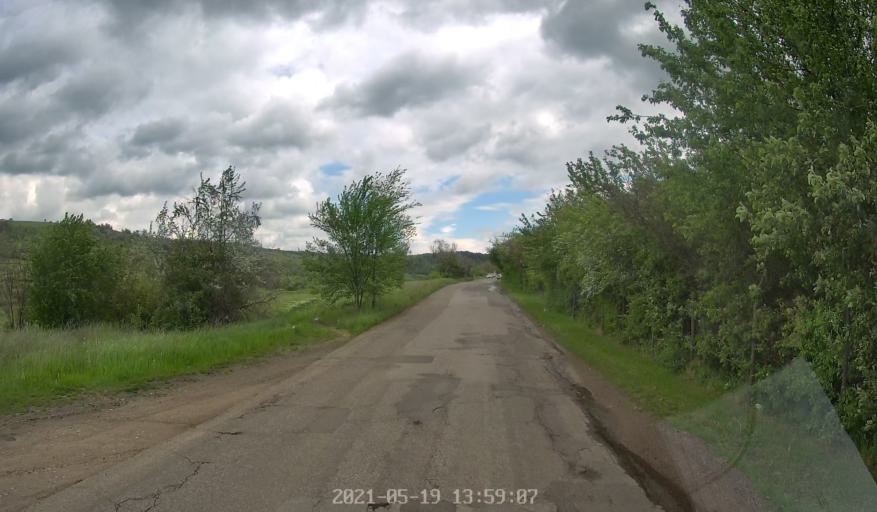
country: MD
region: Chisinau
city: Chisinau
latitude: 47.0417
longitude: 28.9215
